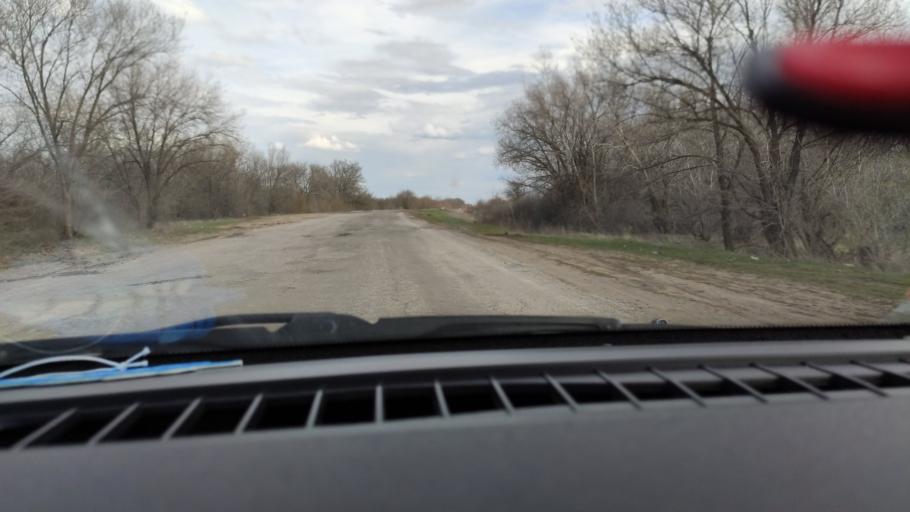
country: RU
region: Saratov
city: Rovnoye
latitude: 51.0428
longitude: 46.0633
